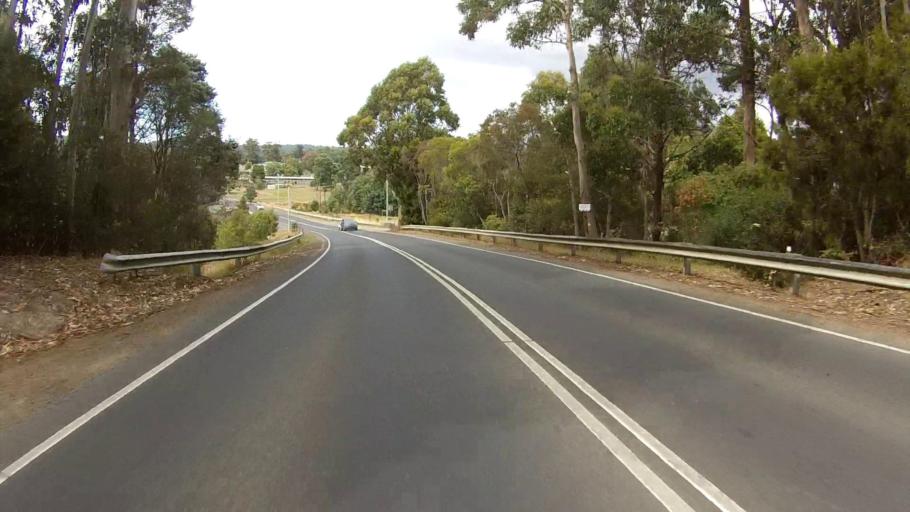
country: AU
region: Tasmania
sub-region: Kingborough
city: Margate
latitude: -43.0623
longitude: 147.2536
